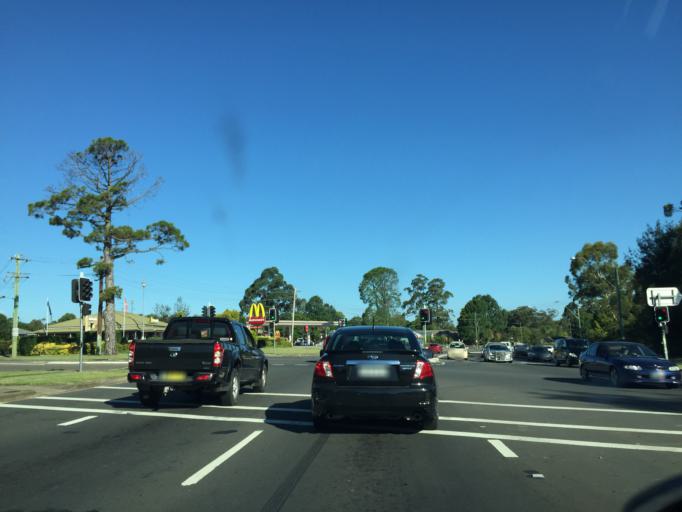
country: AU
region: New South Wales
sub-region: Blue Mountains Municipality
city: Blaxland
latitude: -33.7456
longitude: 150.6124
